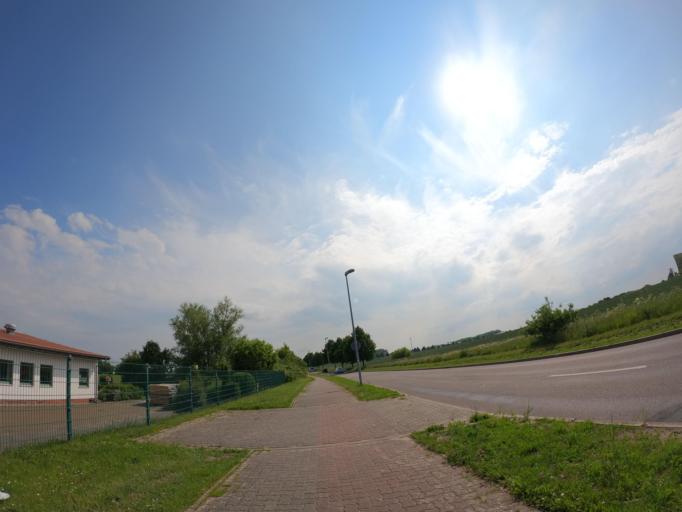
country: DE
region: Mecklenburg-Vorpommern
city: Stralsund
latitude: 54.2856
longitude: 13.0592
